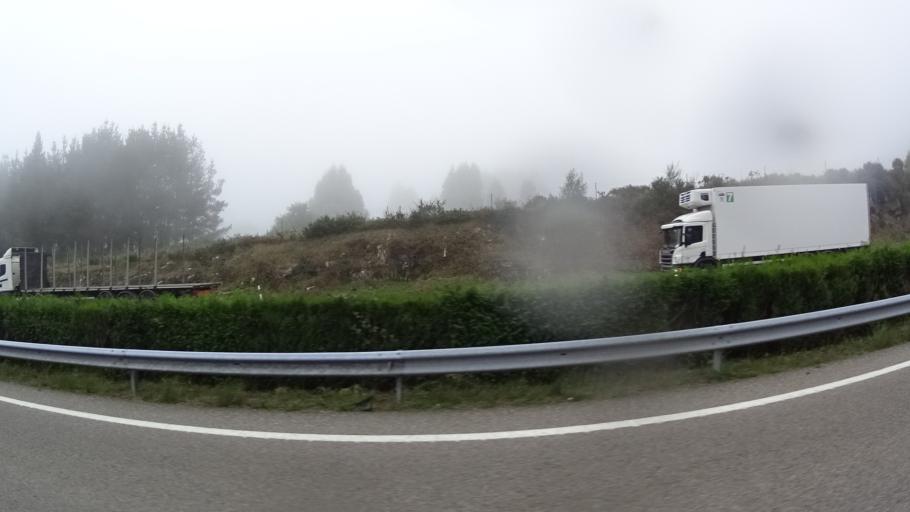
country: ES
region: Galicia
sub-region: Provincia de Lugo
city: Guitiriz
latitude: 43.1887
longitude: -7.8556
